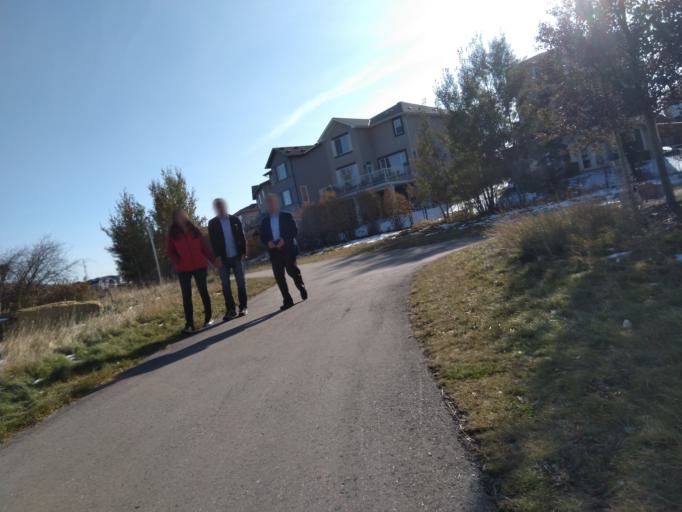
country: CA
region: Alberta
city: Calgary
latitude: 51.1756
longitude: -114.1288
